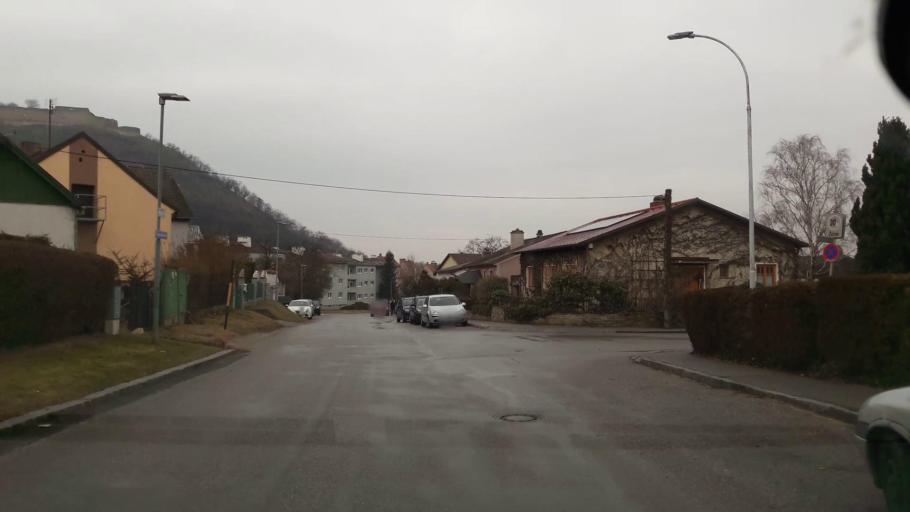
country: AT
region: Lower Austria
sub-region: Politischer Bezirk Bruck an der Leitha
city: Hainburg an der Donau
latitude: 48.1414
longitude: 16.9557
